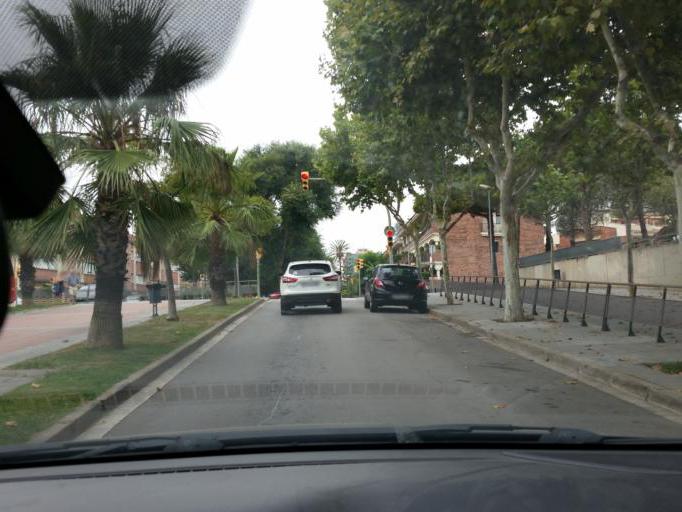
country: ES
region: Catalonia
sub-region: Provincia de Barcelona
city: Vilassar de Mar
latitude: 41.5086
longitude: 2.3924
